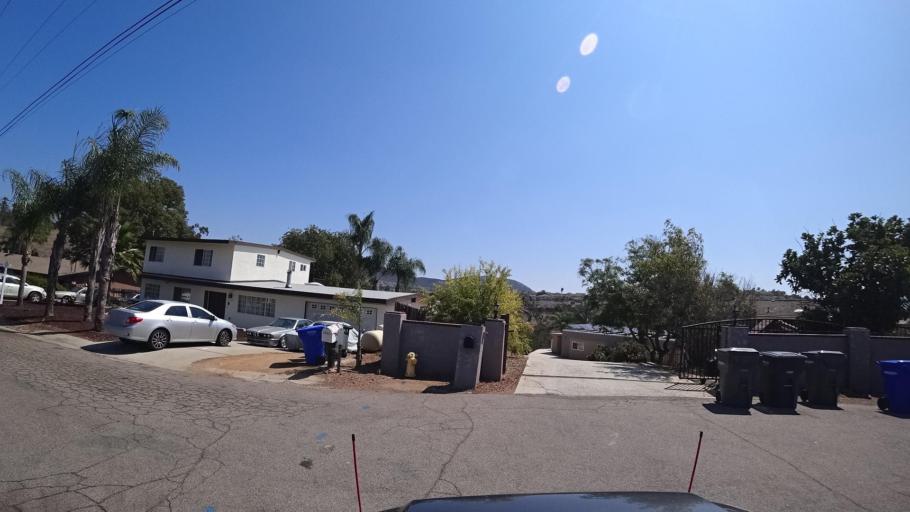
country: US
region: California
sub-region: San Diego County
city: San Marcos
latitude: 33.1647
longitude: -117.1977
